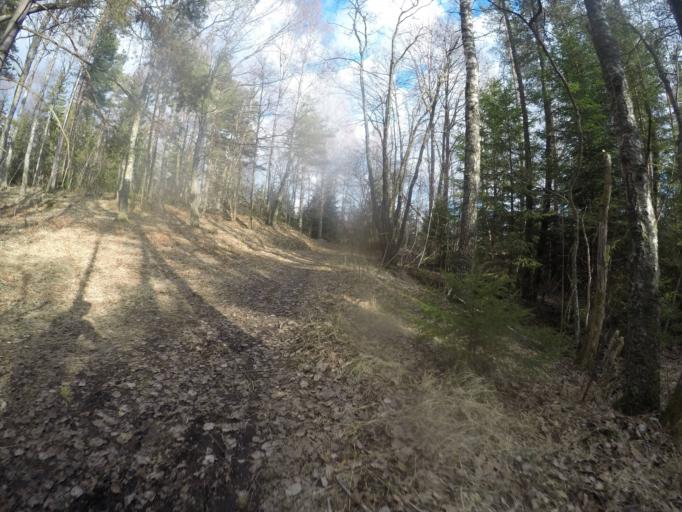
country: SE
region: Soedermanland
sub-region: Eskilstuna Kommun
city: Hallbybrunn
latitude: 59.3876
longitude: 16.3922
